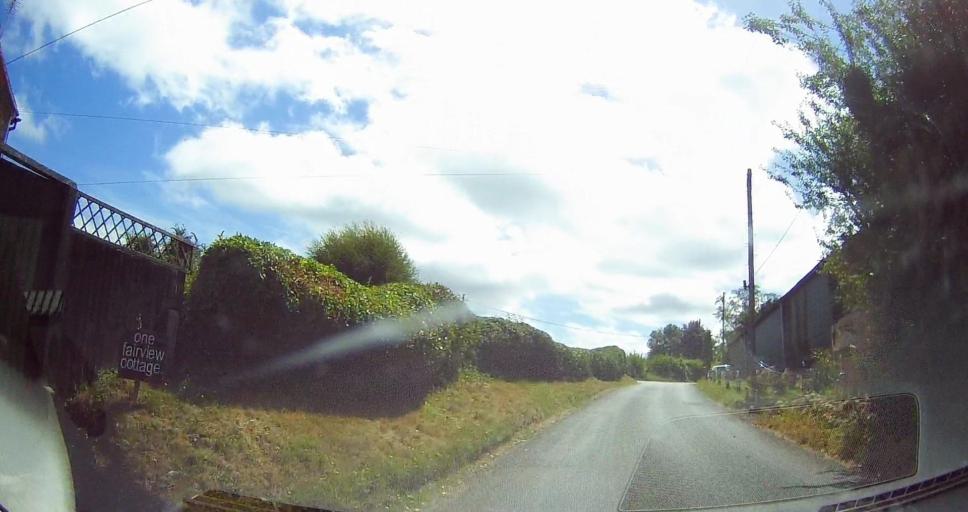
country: GB
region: England
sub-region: Kent
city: Borough Green
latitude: 51.2800
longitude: 0.3189
